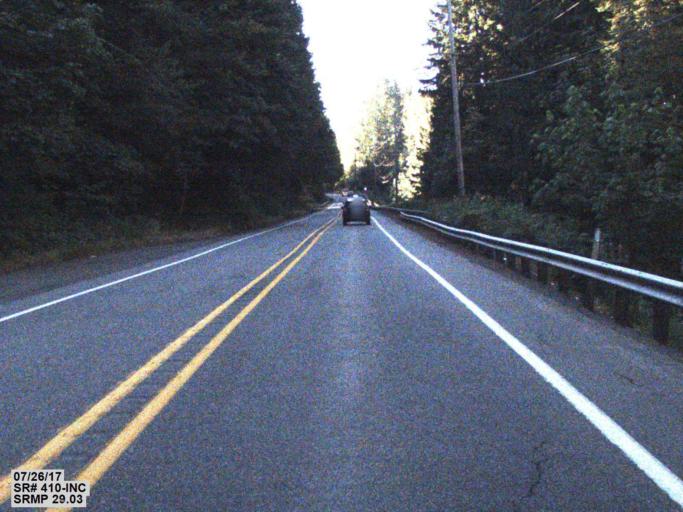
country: US
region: Washington
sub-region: King County
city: Enumclaw
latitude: 47.1699
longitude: -121.9135
